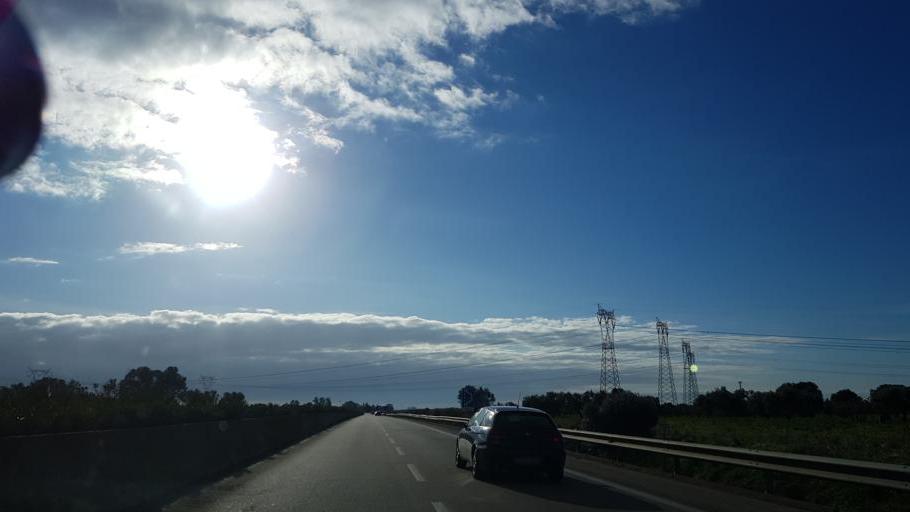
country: IT
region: Apulia
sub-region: Provincia di Brindisi
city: Tuturano
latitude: 40.5638
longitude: 17.9879
